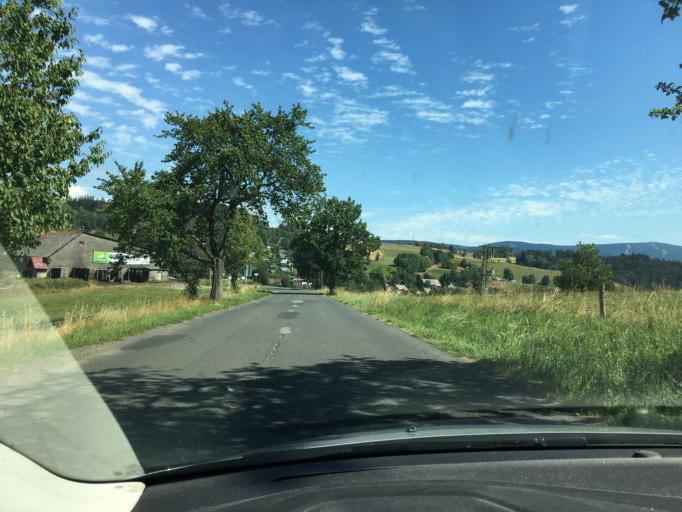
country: CZ
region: Liberecky
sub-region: Okres Semily
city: Vysoke nad Jizerou
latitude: 50.6999
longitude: 15.3859
